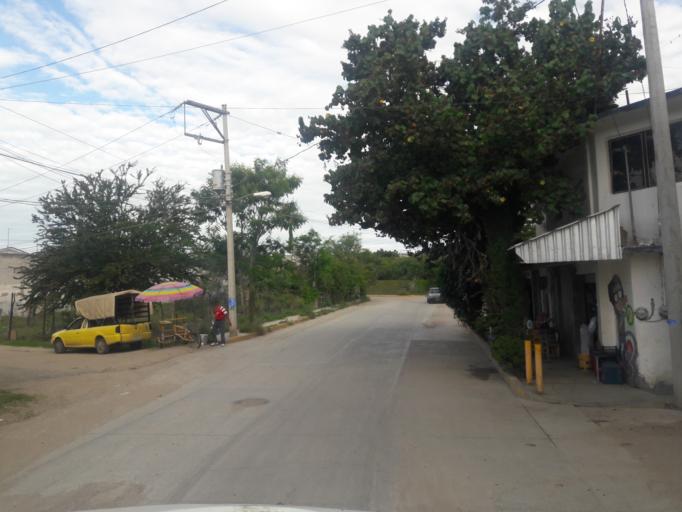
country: MX
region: Oaxaca
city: Ciudad de Huajuapam de Leon
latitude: 17.8055
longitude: -97.7868
